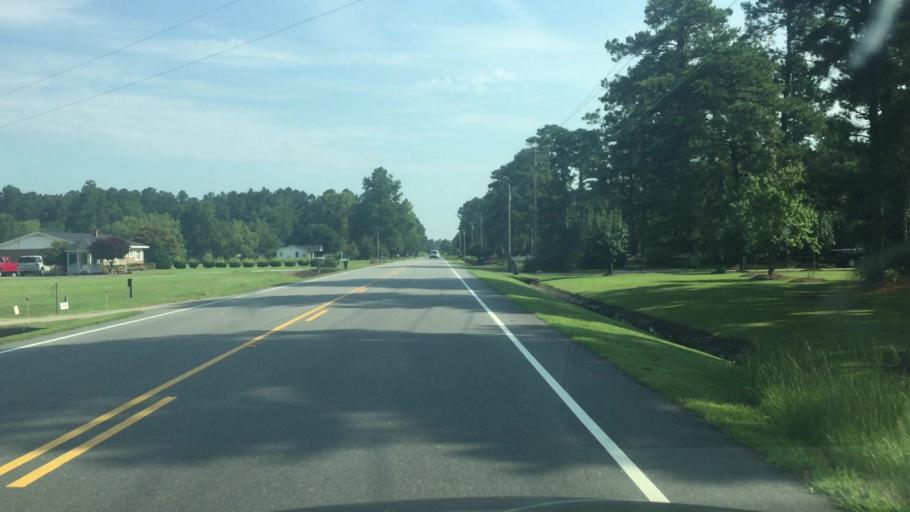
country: US
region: North Carolina
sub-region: Columbus County
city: Chadbourn
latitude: 34.2359
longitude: -78.8236
